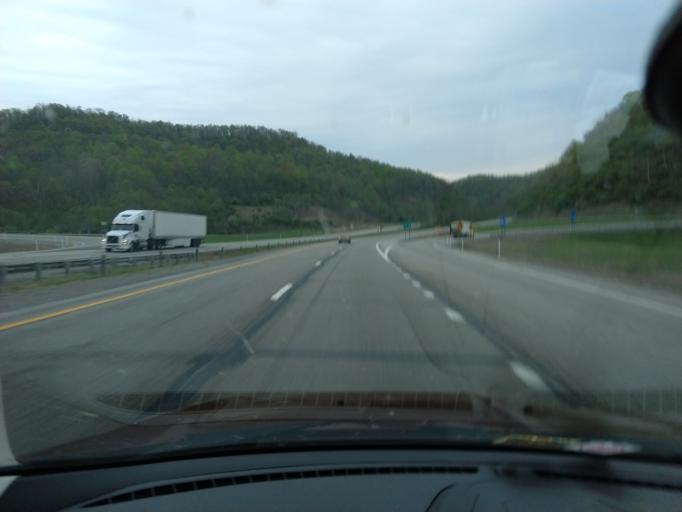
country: US
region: West Virginia
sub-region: Lewis County
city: Weston
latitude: 39.0144
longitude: -80.4704
